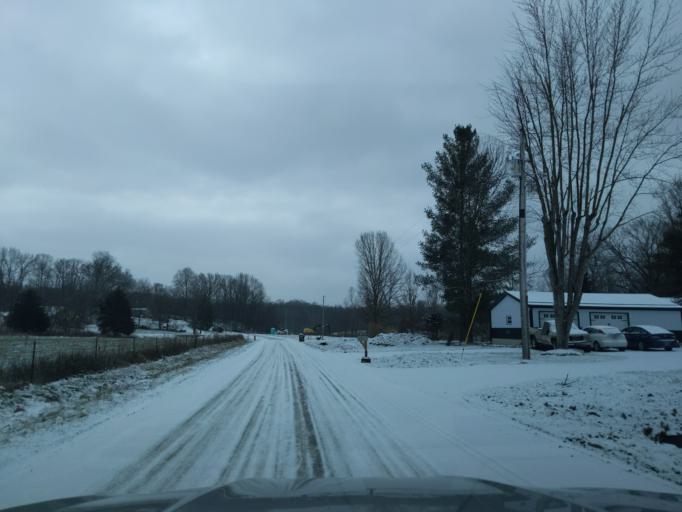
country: US
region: Indiana
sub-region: Decatur County
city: Westport
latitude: 39.2066
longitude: -85.5226
